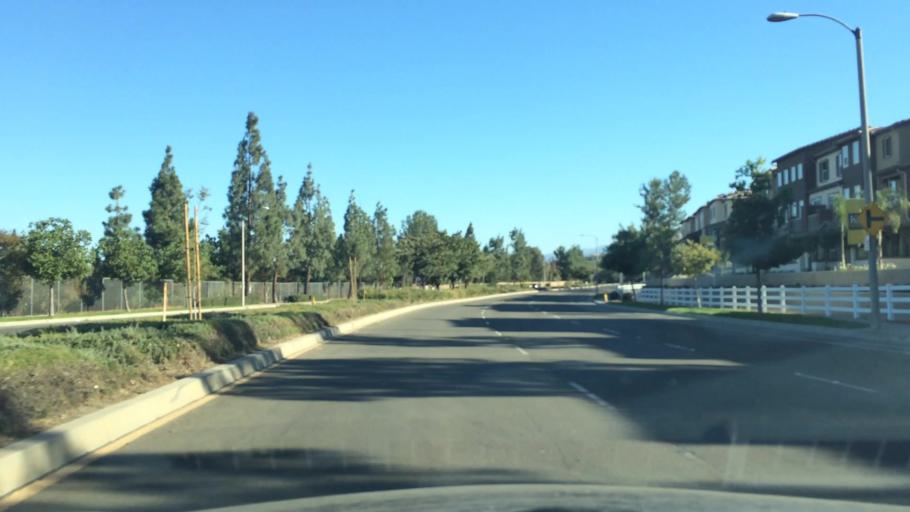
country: US
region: California
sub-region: San Bernardino County
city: Los Serranos
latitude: 33.9607
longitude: -117.6919
